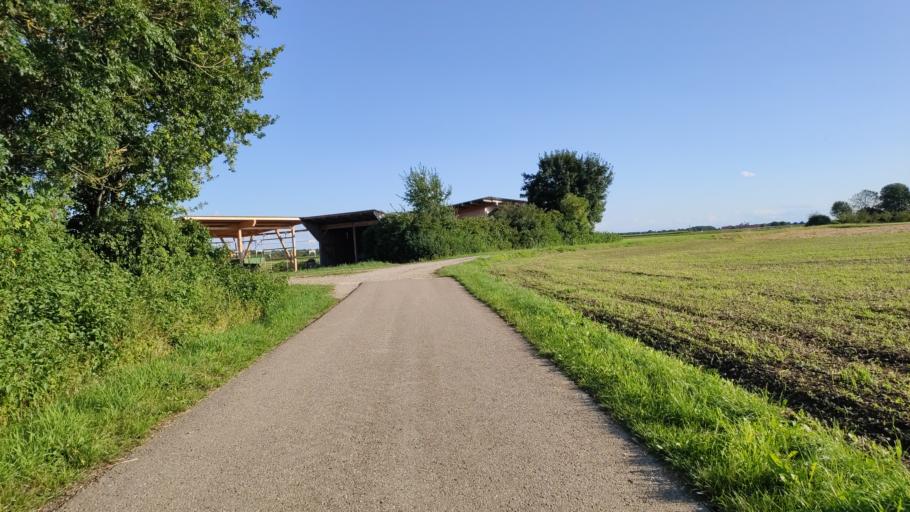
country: DE
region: Bavaria
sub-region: Swabia
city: Oberottmarshausen
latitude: 48.2290
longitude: 10.8593
